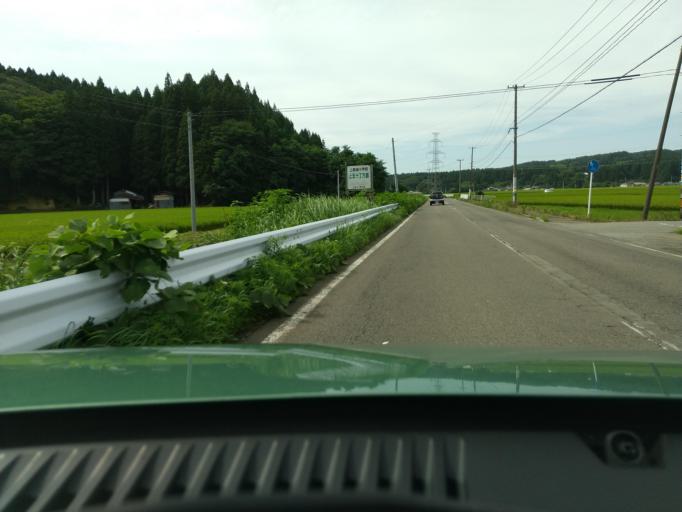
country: JP
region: Akita
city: Akita
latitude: 39.7872
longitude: 140.1213
